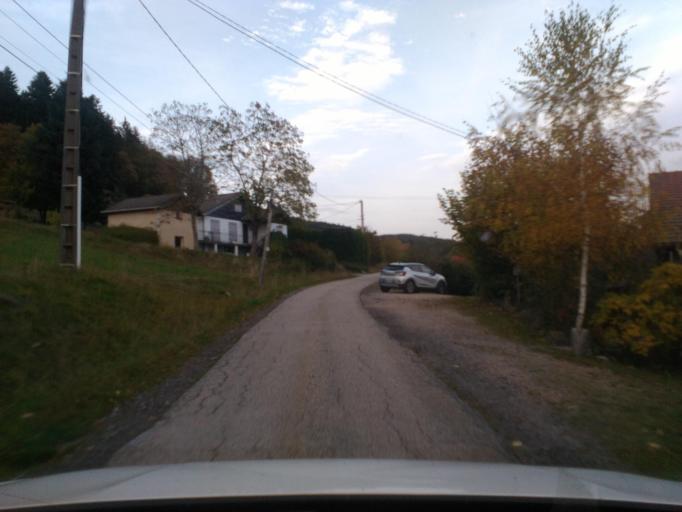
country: FR
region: Lorraine
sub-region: Departement des Vosges
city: Le Tholy
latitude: 48.0872
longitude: 6.7873
